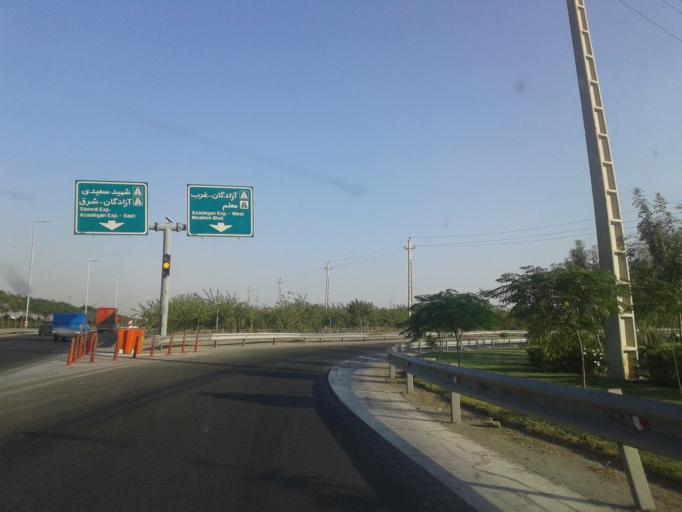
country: IR
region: Tehran
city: Eslamshahr
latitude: 35.6496
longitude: 51.2742
